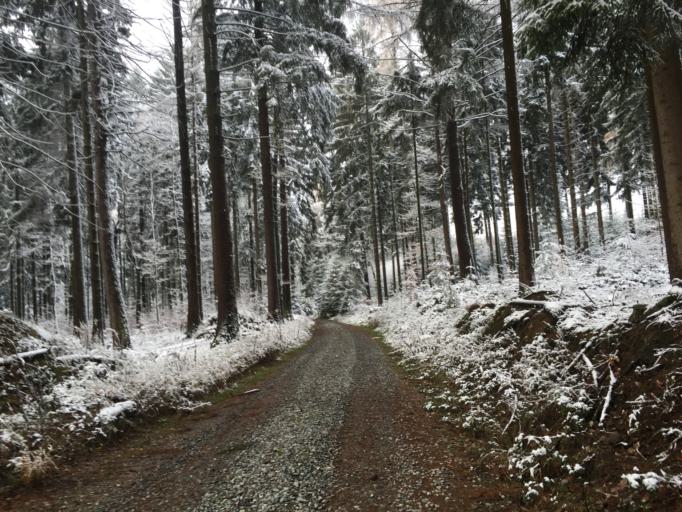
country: DE
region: Hesse
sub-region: Regierungsbezirk Darmstadt
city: Wald-Michelbach
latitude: 49.5893
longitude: 8.8833
